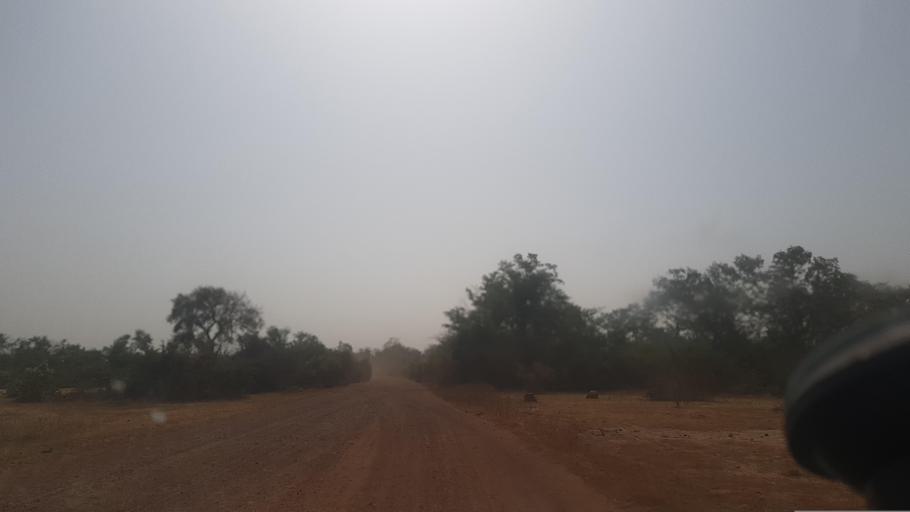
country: ML
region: Segou
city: Baroueli
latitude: 13.0759
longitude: -6.4832
